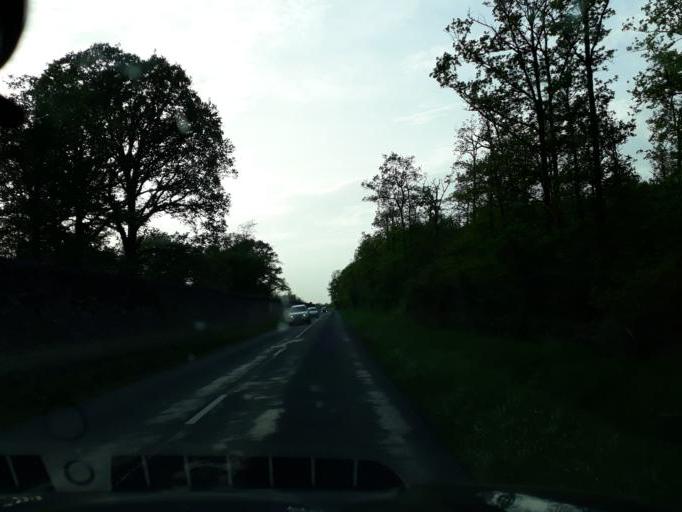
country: FR
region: Centre
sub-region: Departement du Loir-et-Cher
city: Muides-sur-Loire
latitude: 47.6593
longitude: 1.5431
